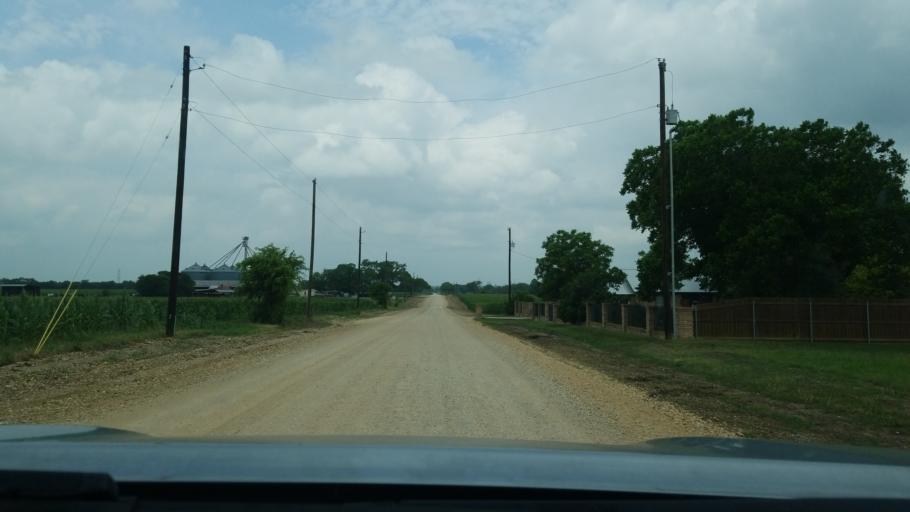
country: US
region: Texas
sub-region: Guadalupe County
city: Geronimo
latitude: 29.6846
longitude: -98.0031
